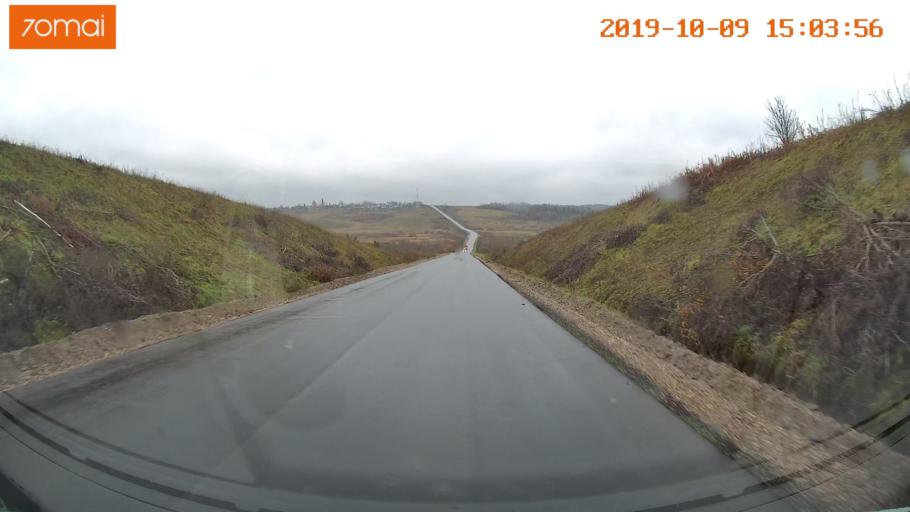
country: RU
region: Kostroma
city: Chistyye Bory
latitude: 58.2648
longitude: 41.6717
